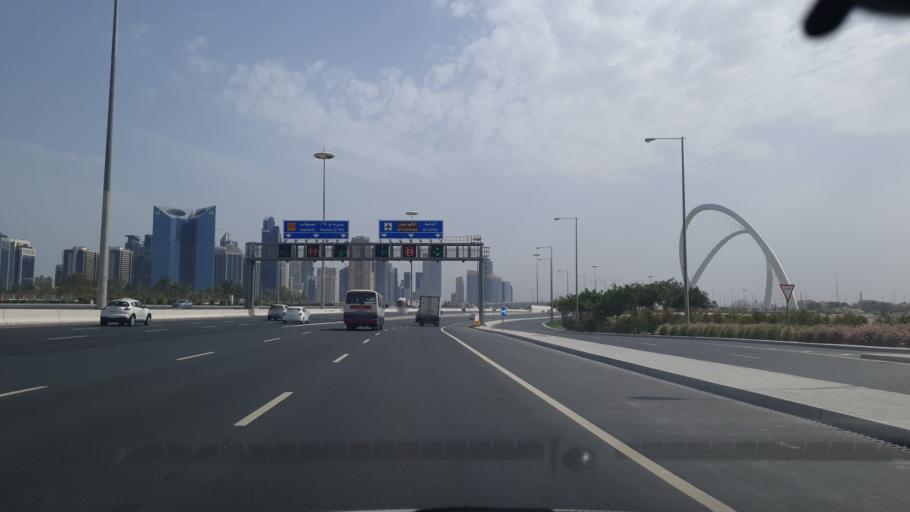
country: QA
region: Baladiyat ad Dawhah
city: Doha
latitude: 25.3410
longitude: 51.5203
